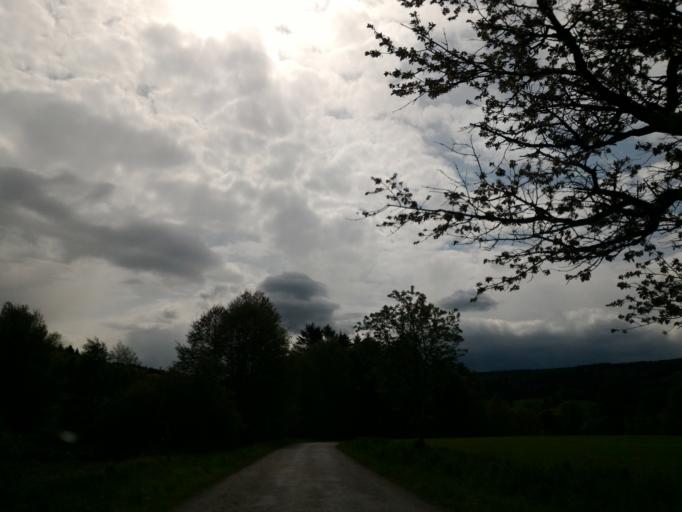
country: CZ
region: Vysocina
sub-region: Okres Havlickuv Brod
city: Svetla nad Sazavou
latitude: 49.6326
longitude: 15.3613
